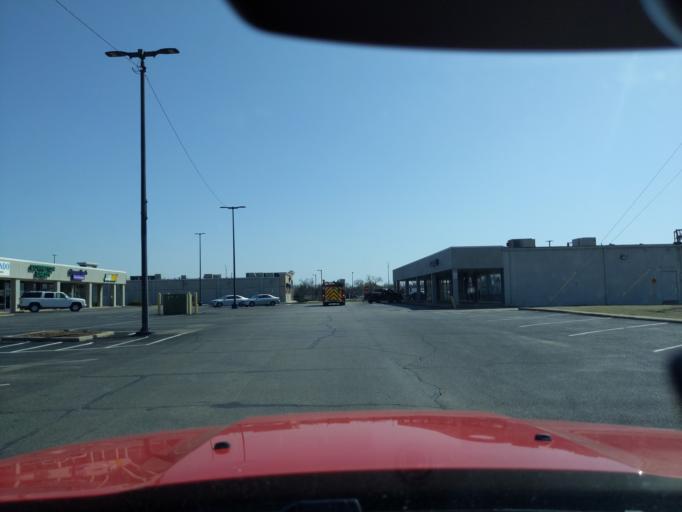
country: US
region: Oklahoma
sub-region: Cleveland County
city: Moore
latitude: 35.3455
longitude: -97.4966
